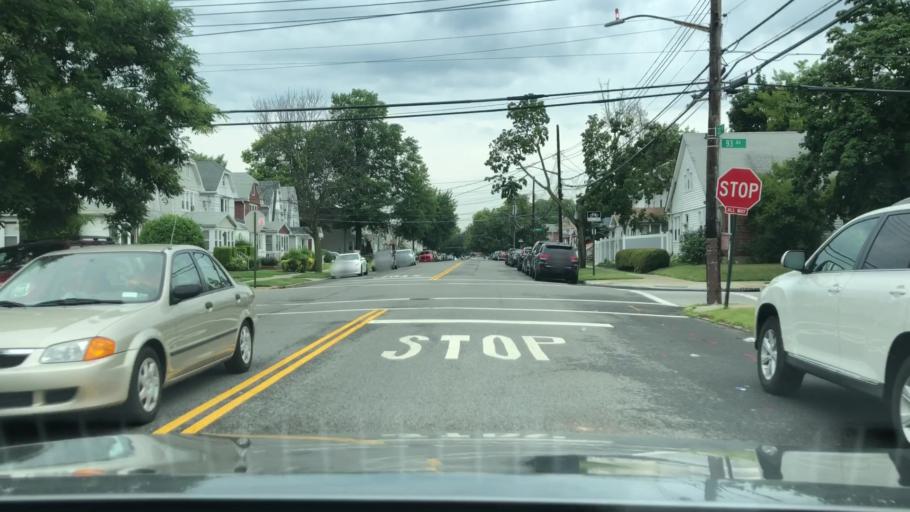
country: US
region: New York
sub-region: Nassau County
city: Bellerose Terrace
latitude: 40.7230
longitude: -73.7335
